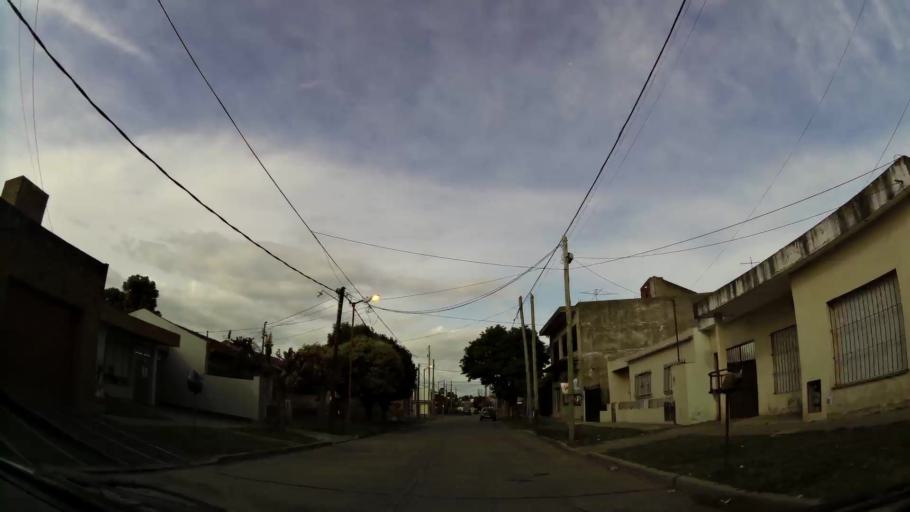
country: AR
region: Buenos Aires
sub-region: Partido de Quilmes
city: Quilmes
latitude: -34.7397
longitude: -58.2722
